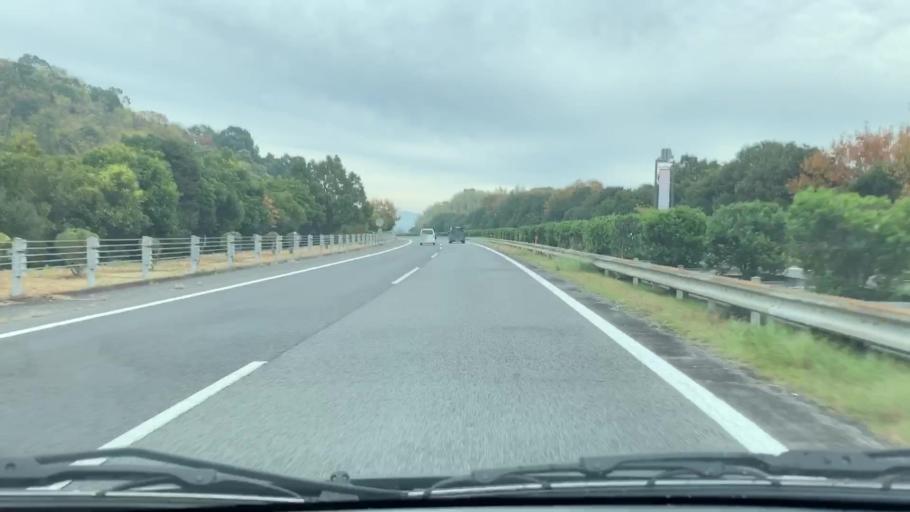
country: JP
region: Saga Prefecture
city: Saga-shi
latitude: 33.2873
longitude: 130.1591
